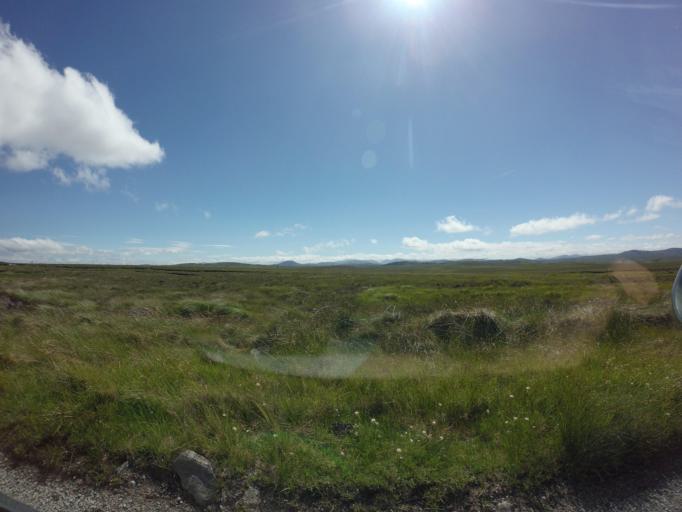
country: GB
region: Scotland
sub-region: Eilean Siar
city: Isle of Lewis
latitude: 58.1859
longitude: -6.6801
